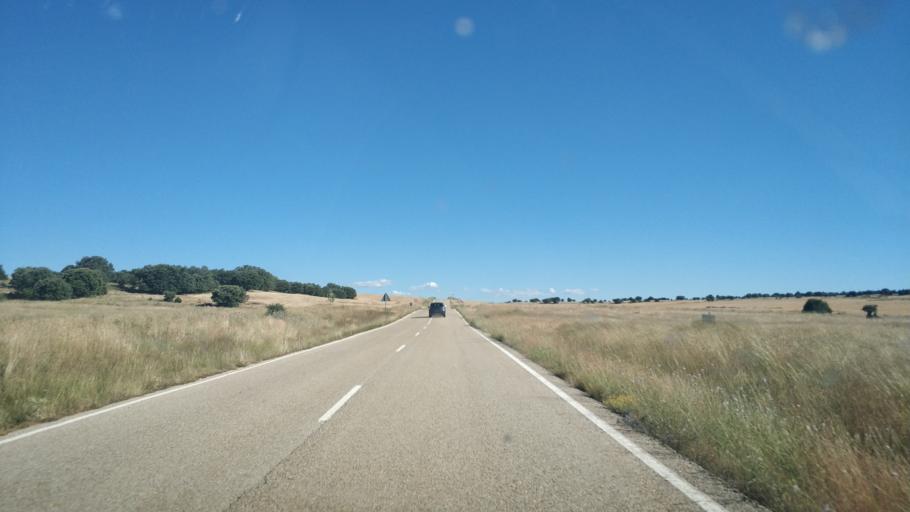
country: ES
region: Castille and Leon
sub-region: Provincia de Soria
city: Montejo de Tiermes
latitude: 41.3962
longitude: -3.1991
